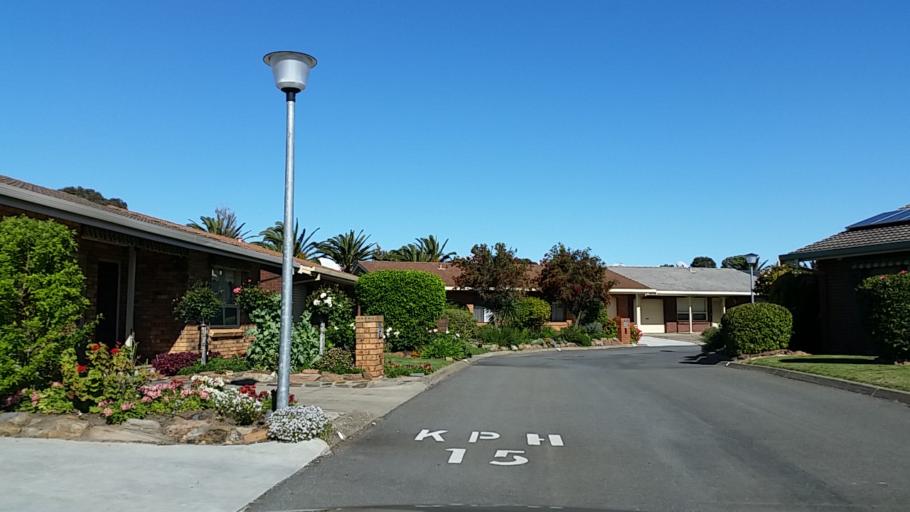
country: AU
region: South Australia
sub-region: Charles Sturt
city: West Lakes Shore
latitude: -34.8710
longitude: 138.4894
